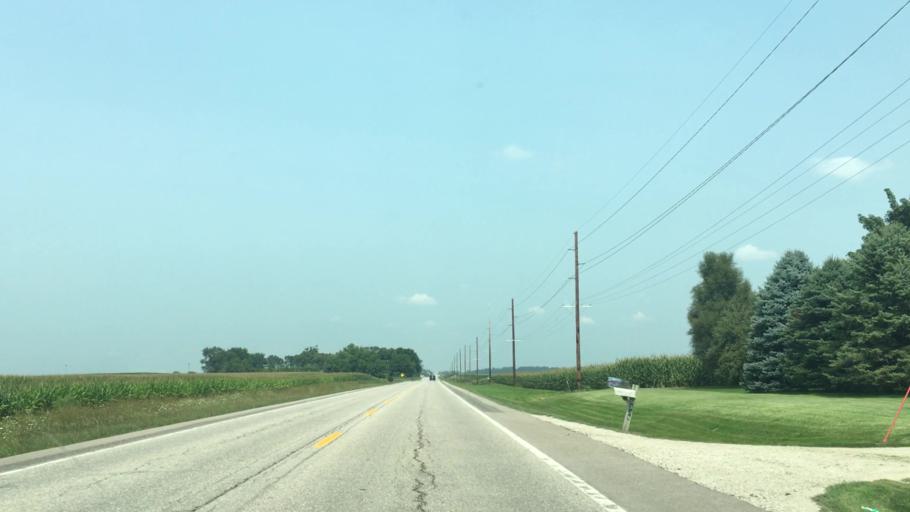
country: US
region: Iowa
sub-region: Benton County
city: Urbana
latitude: 42.2505
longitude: -91.8909
